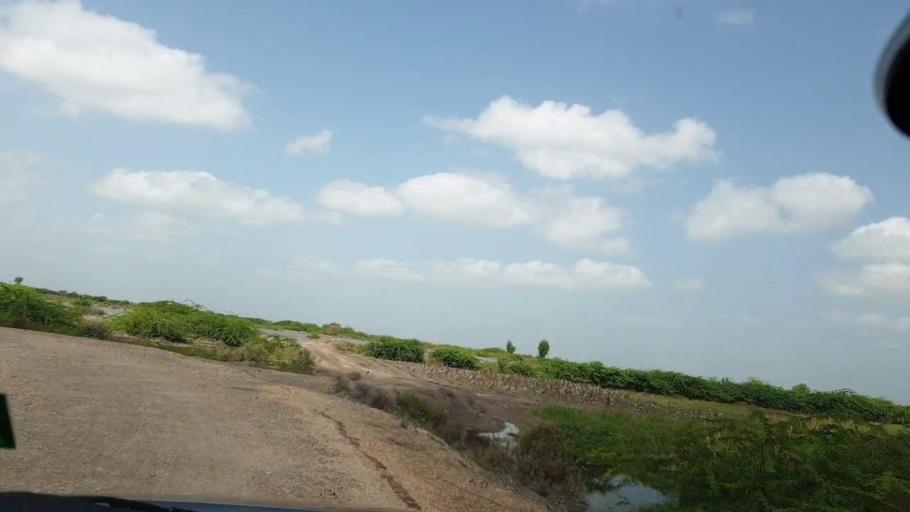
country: PK
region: Sindh
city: Kadhan
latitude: 24.5842
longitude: 69.1533
